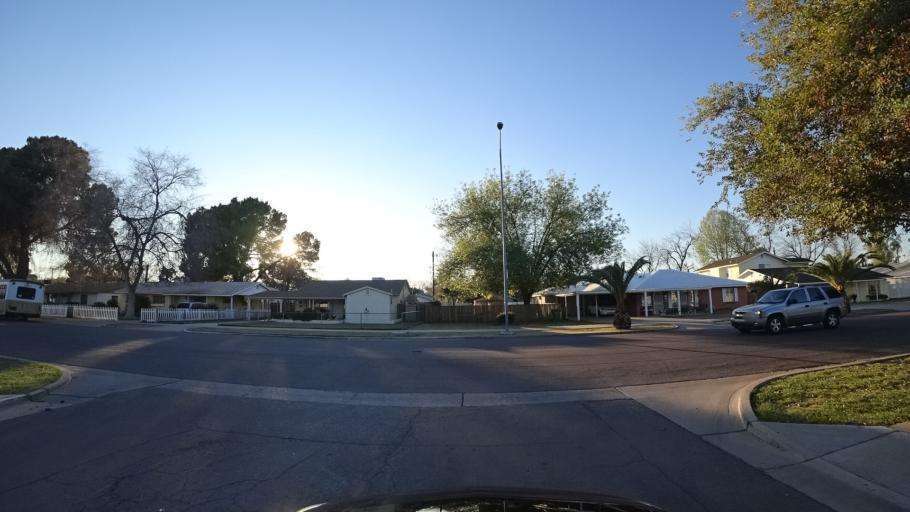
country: US
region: Arizona
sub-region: Maricopa County
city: Mesa
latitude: 33.4303
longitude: -111.8355
